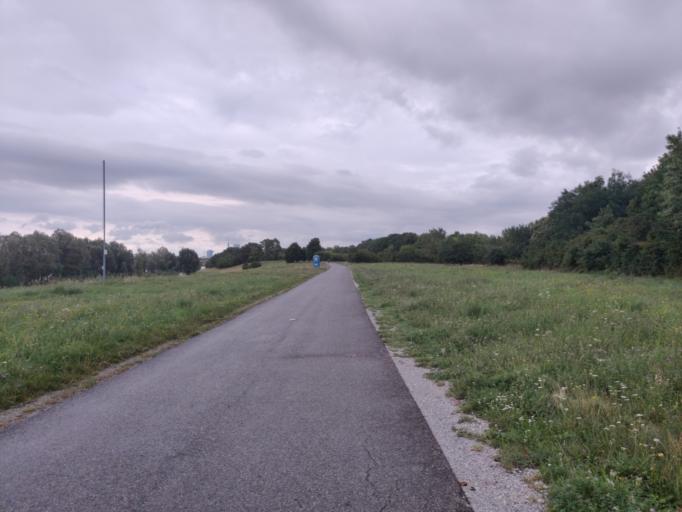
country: AT
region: Lower Austria
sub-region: Politischer Bezirk Korneuburg
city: Langenzersdorf
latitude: 48.2763
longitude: 16.3629
